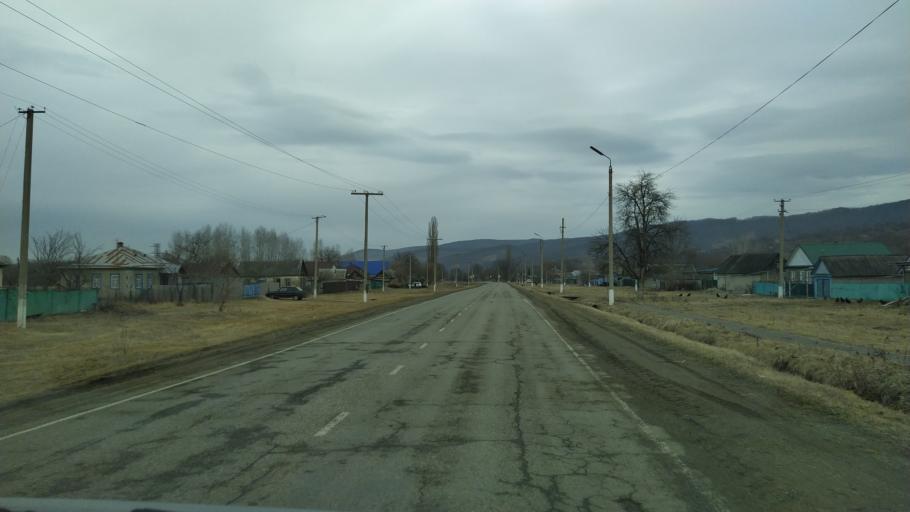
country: RU
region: Krasnodarskiy
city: Peredovaya
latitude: 44.1330
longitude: 41.4952
